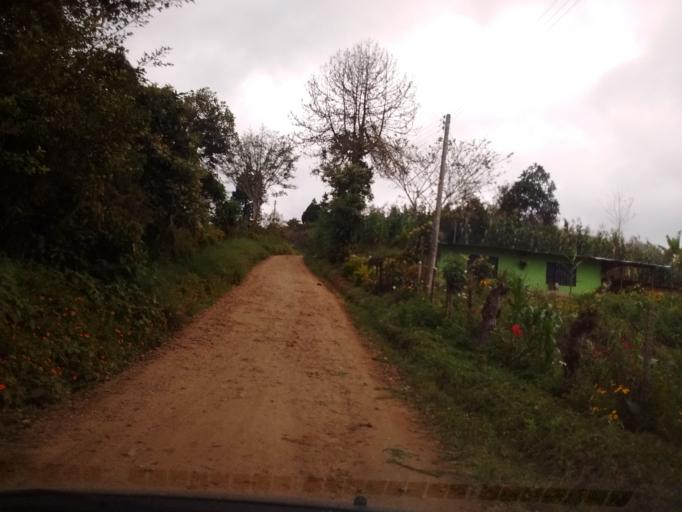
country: CO
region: Huila
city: San Agustin
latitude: 1.9054
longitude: -76.3008
